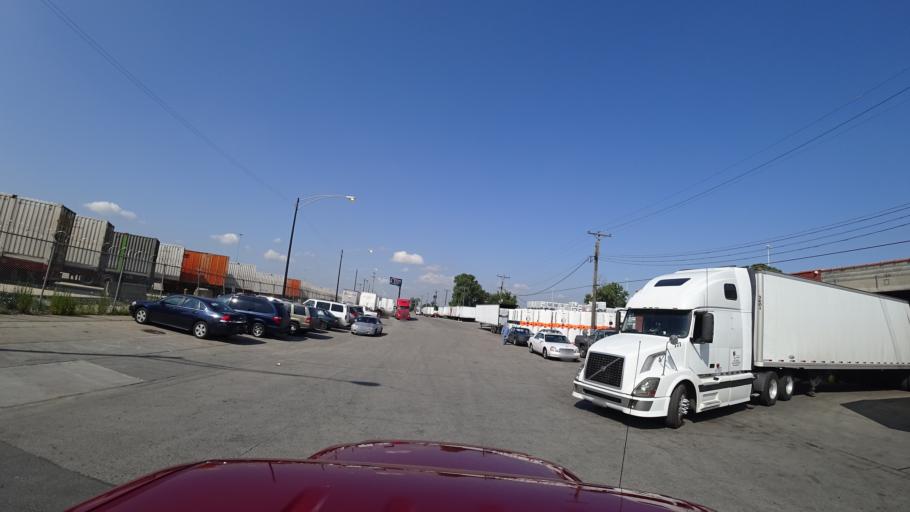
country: US
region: Illinois
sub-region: Cook County
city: Cicero
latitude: 41.8241
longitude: -87.7158
